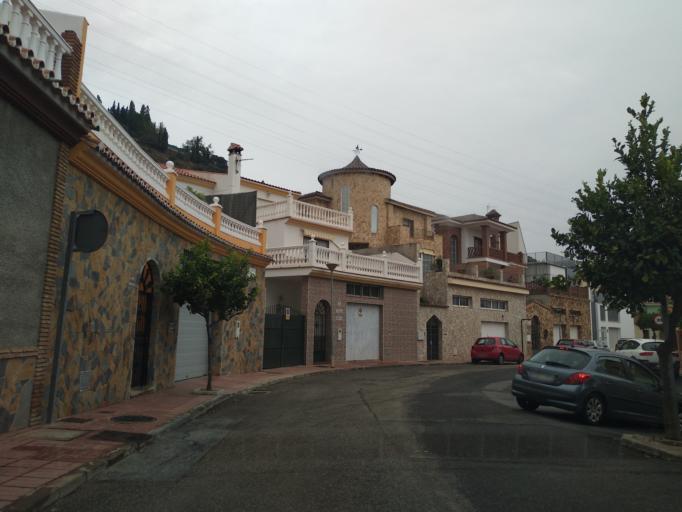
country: ES
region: Andalusia
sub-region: Provincia de Malaga
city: Malaga
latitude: 36.7423
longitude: -4.4754
